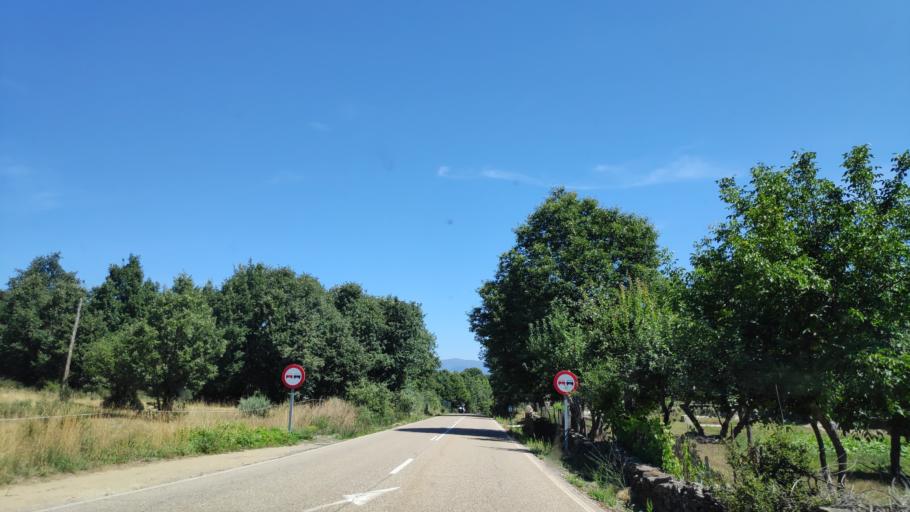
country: ES
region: Castille and Leon
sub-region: Provincia de Zamora
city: Cobreros
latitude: 42.0330
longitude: -6.6759
